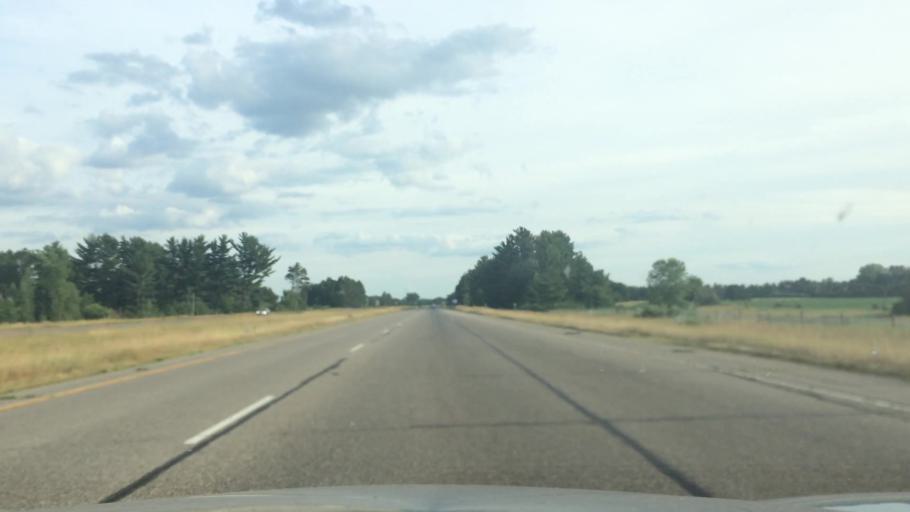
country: US
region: Wisconsin
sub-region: Portage County
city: Plover
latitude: 44.2086
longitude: -89.5242
